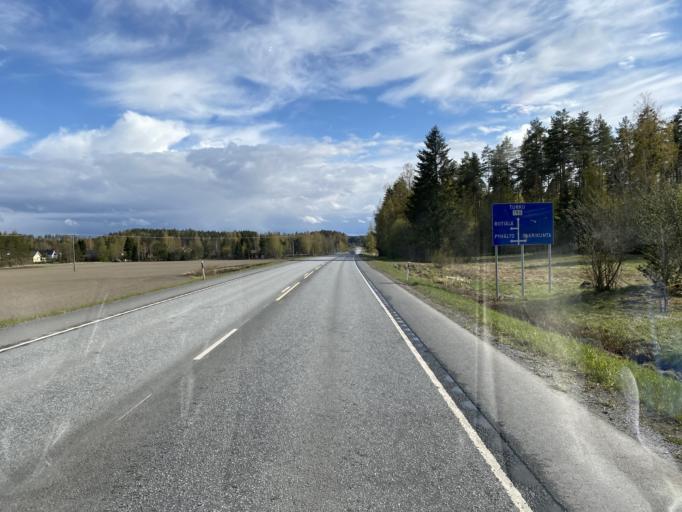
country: FI
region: Pirkanmaa
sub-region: Tampere
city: Lempaeaelae
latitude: 61.2706
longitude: 23.7470
